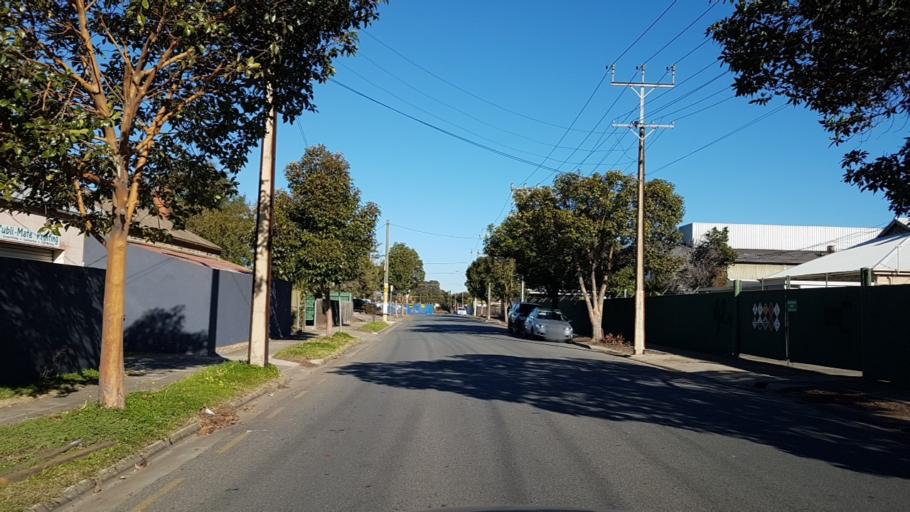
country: AU
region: South Australia
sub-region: City of West Torrens
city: Plympton
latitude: -34.9590
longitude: 138.5455
